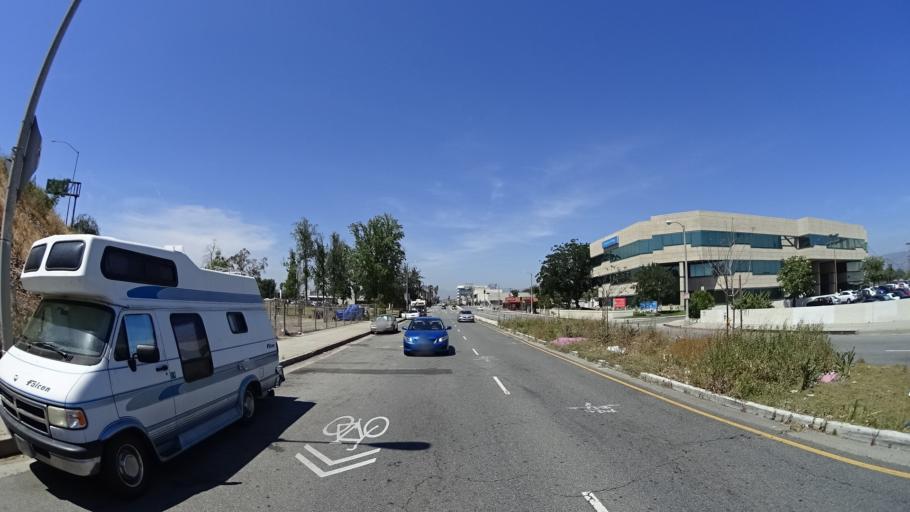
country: US
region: California
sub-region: Los Angeles County
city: North Hollywood
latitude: 34.1822
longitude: -118.3961
